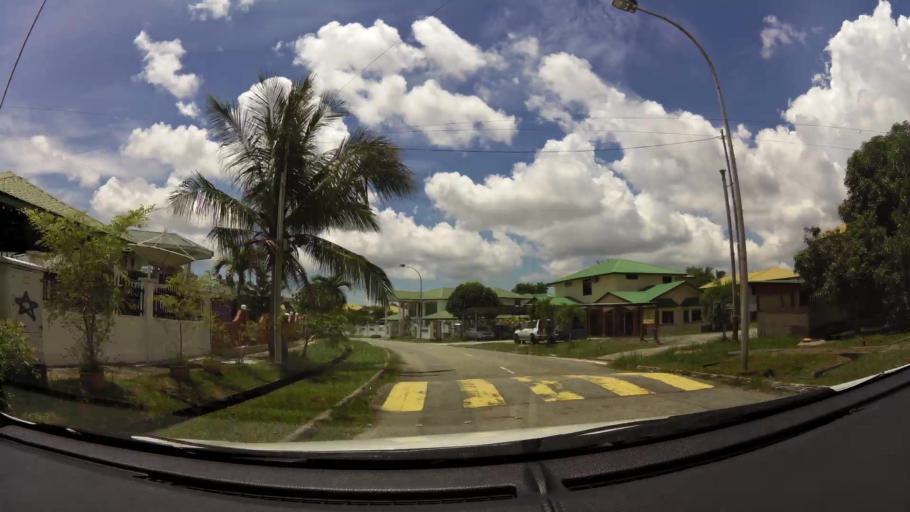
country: BN
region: Brunei and Muara
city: Bandar Seri Begawan
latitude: 4.9597
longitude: 114.9151
